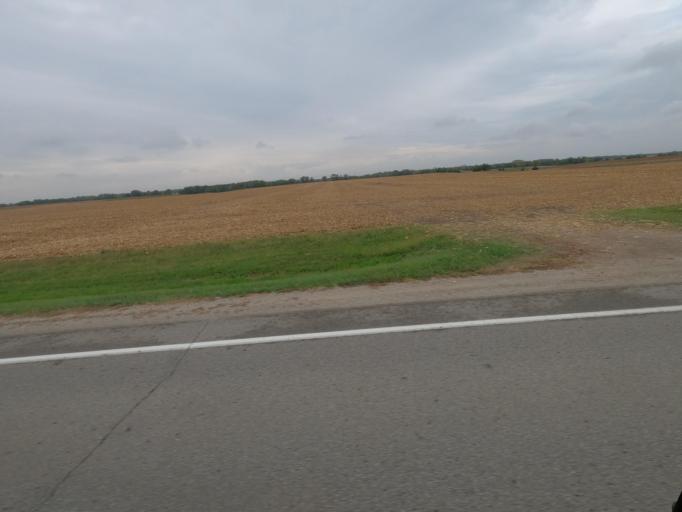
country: US
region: Iowa
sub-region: Van Buren County
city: Keosauqua
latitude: 40.8135
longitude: -91.8794
